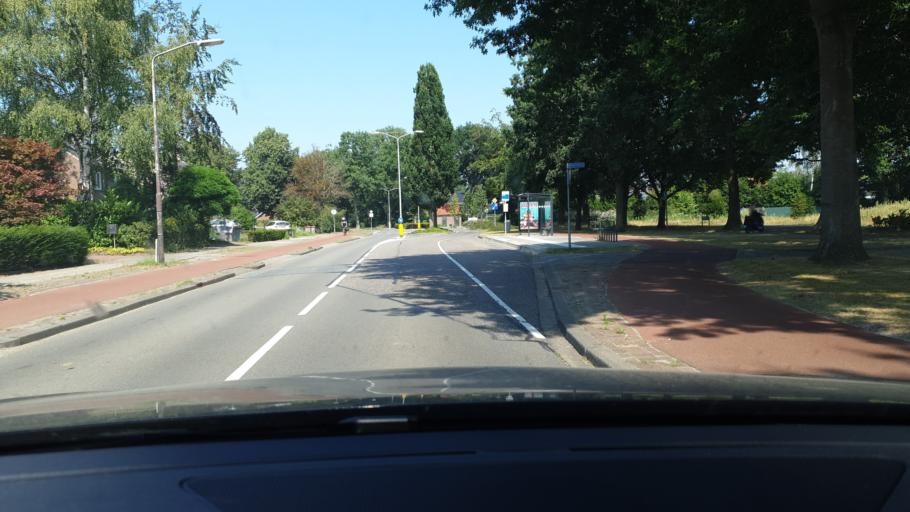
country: NL
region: North Brabant
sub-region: Gemeente Veldhoven
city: Oerle
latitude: 51.4123
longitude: 5.3853
